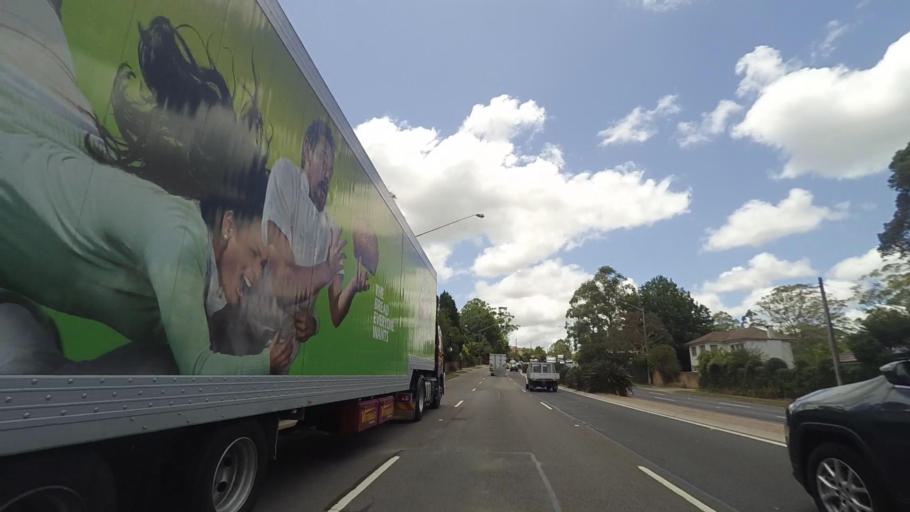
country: AU
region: New South Wales
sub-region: The Hills Shire
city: West Pennant
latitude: -33.7431
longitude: 151.0548
